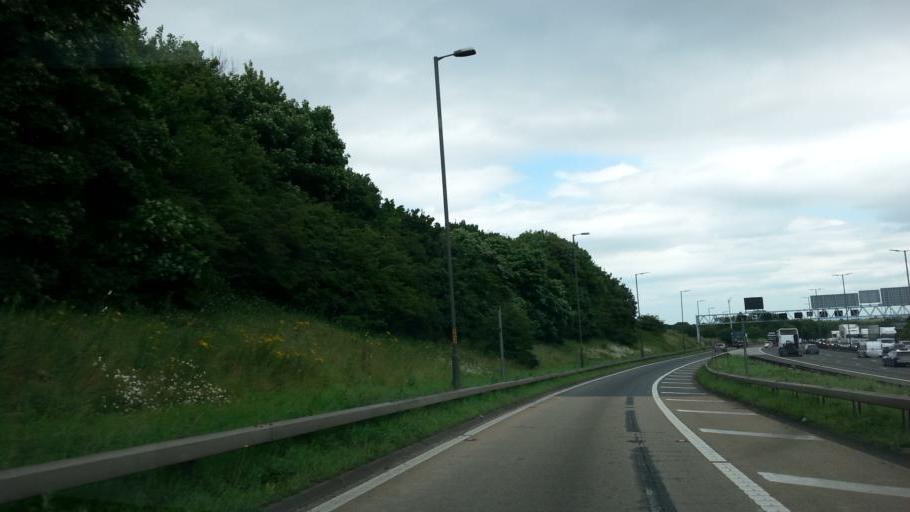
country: GB
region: England
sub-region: Walsall
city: Aldridge
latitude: 52.5533
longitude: -1.9297
